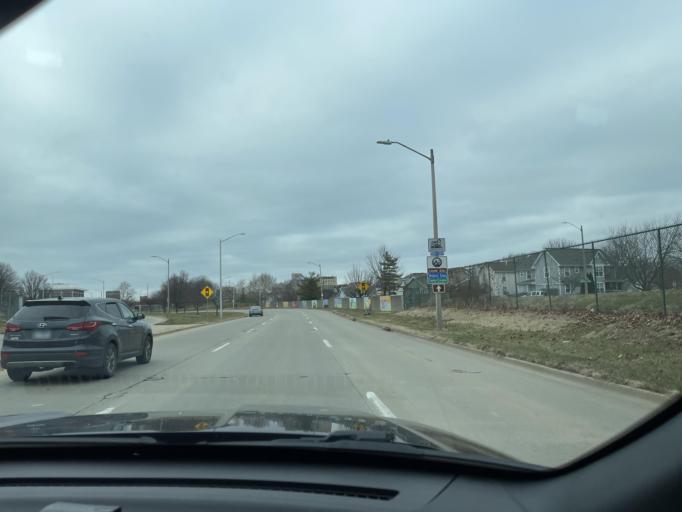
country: US
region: Illinois
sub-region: Sangamon County
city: Springfield
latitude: 39.8035
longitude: -89.6357
